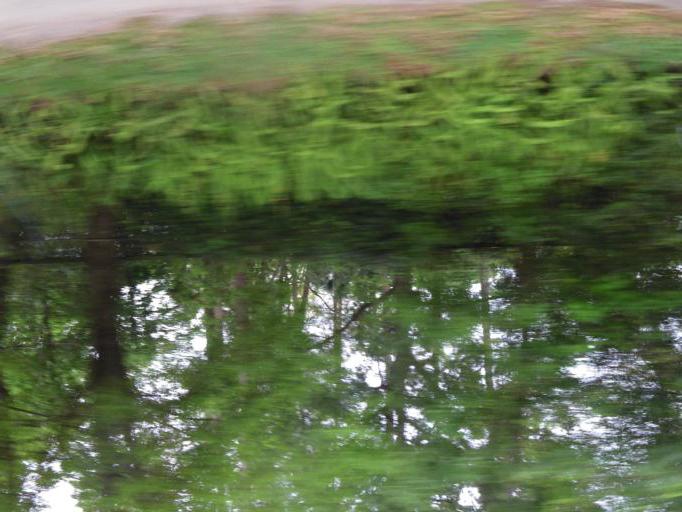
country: US
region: Florida
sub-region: Duval County
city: Jacksonville
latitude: 30.3168
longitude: -81.5659
